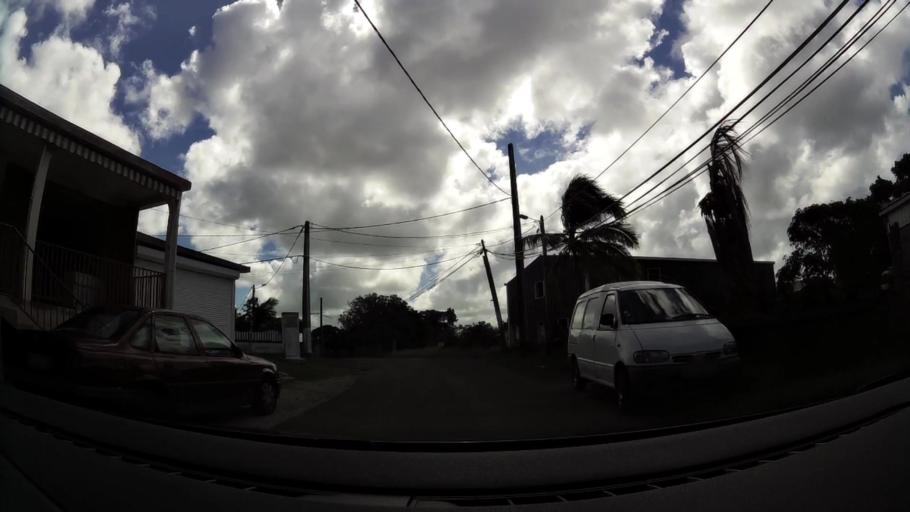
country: GP
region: Guadeloupe
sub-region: Guadeloupe
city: Anse-Bertrand
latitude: 16.4667
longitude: -61.5049
